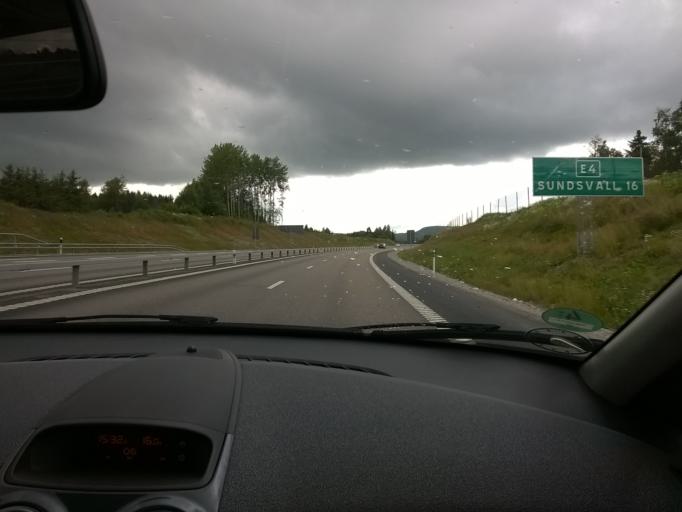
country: SE
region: Vaesternorrland
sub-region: Sundsvalls Kommun
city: Nolby
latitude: 62.2690
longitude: 17.3470
